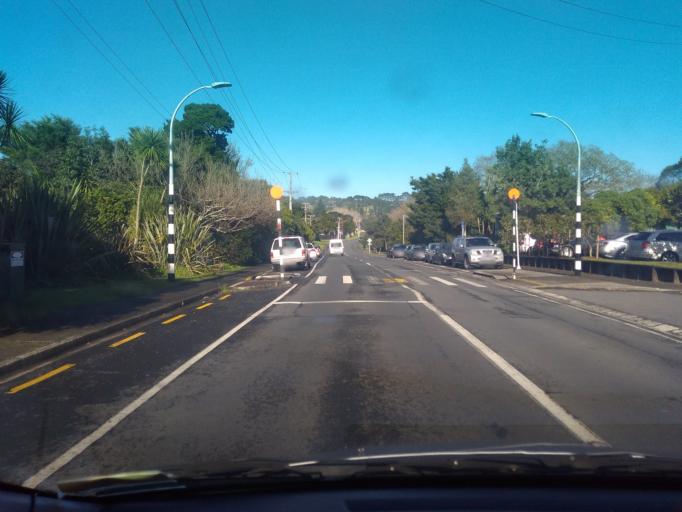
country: NZ
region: Auckland
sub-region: Auckland
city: Muriwai Beach
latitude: -36.7703
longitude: 174.4916
